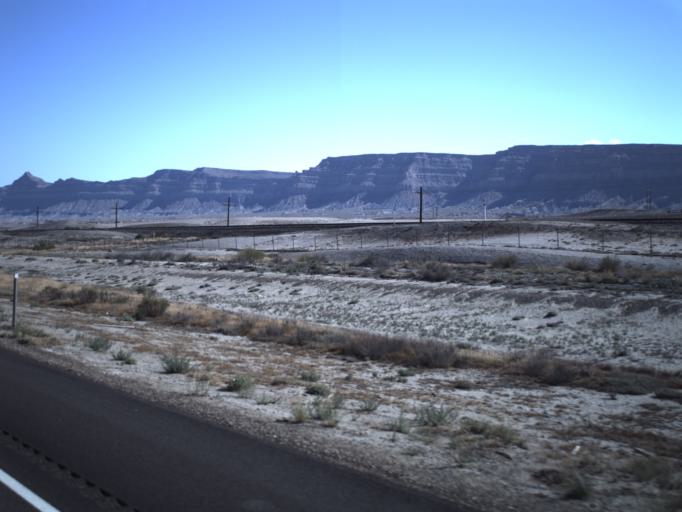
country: US
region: Utah
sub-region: Carbon County
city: East Carbon City
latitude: 39.0737
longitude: -110.3161
